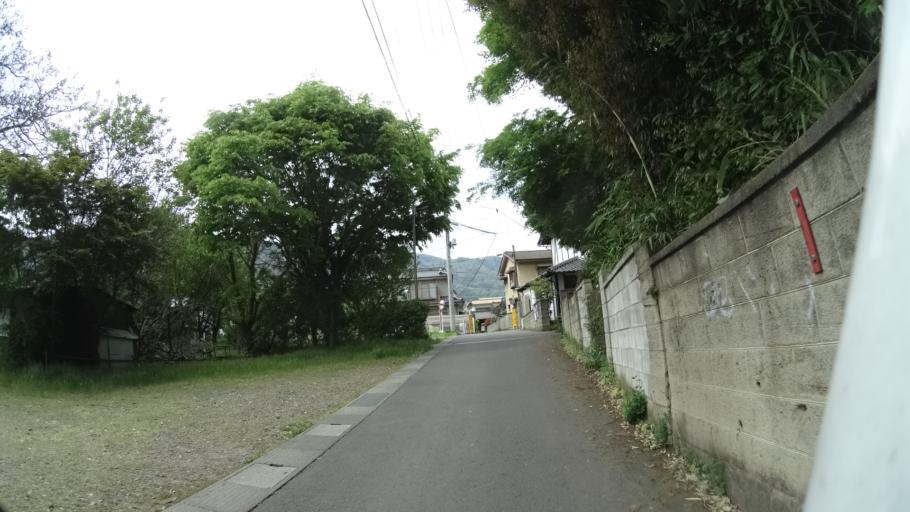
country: JP
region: Nagano
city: Ueda
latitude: 36.4639
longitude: 138.1828
